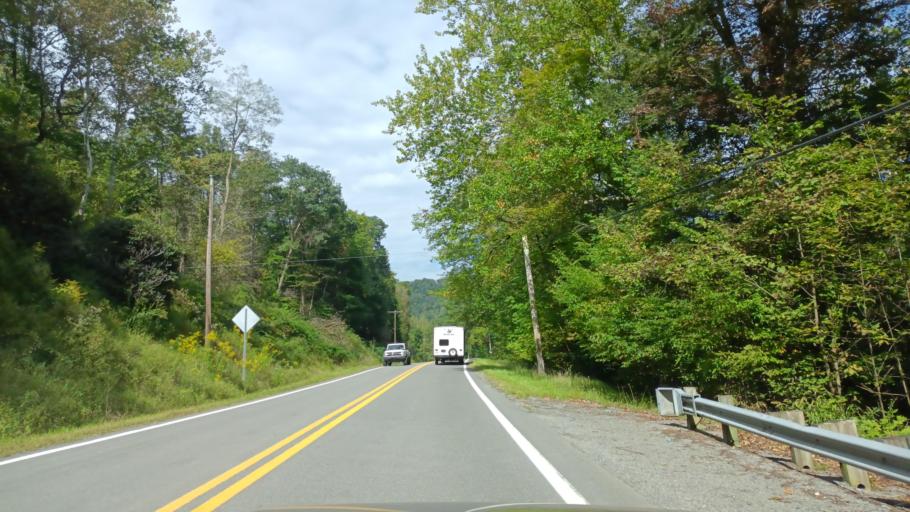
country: US
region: West Virginia
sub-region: Preston County
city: Kingwood
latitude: 39.3206
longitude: -79.6583
